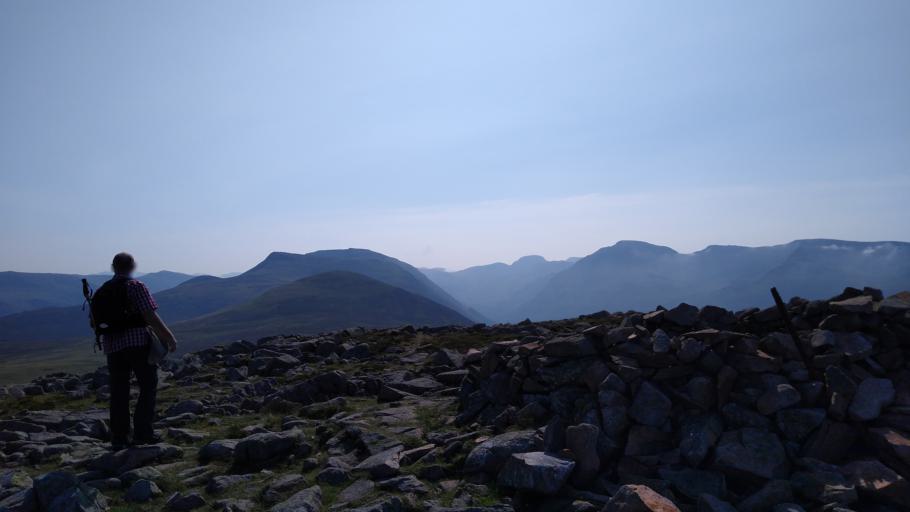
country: GB
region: England
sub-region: Cumbria
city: Cockermouth
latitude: 54.5351
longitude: -3.3555
